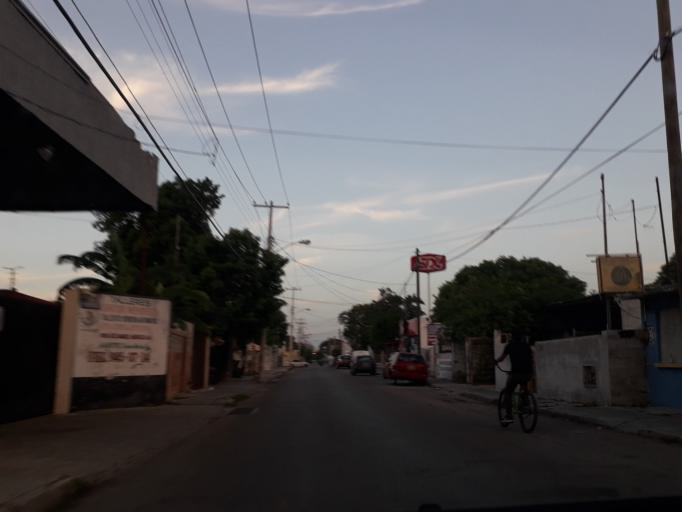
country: MX
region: Yucatan
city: Merida
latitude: 20.9852
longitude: -89.6540
